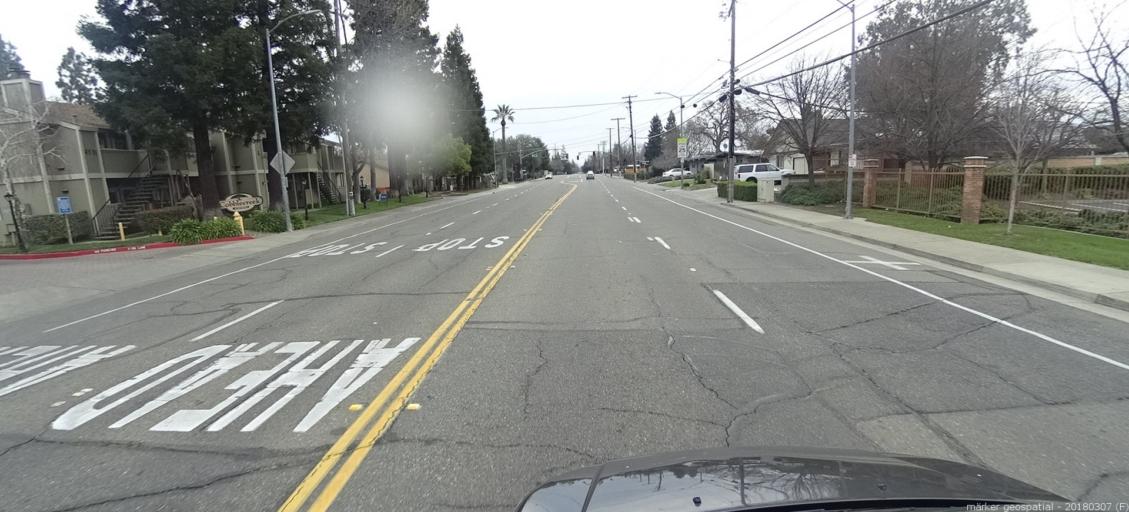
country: US
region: California
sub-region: Sacramento County
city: Carmichael
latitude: 38.6283
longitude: -121.3541
